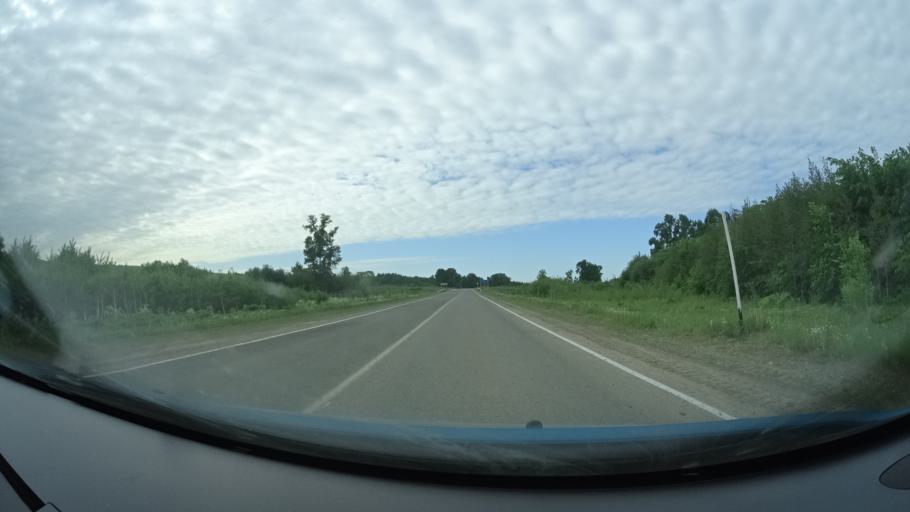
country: RU
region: Perm
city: Kuyeda
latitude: 56.5102
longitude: 55.6266
